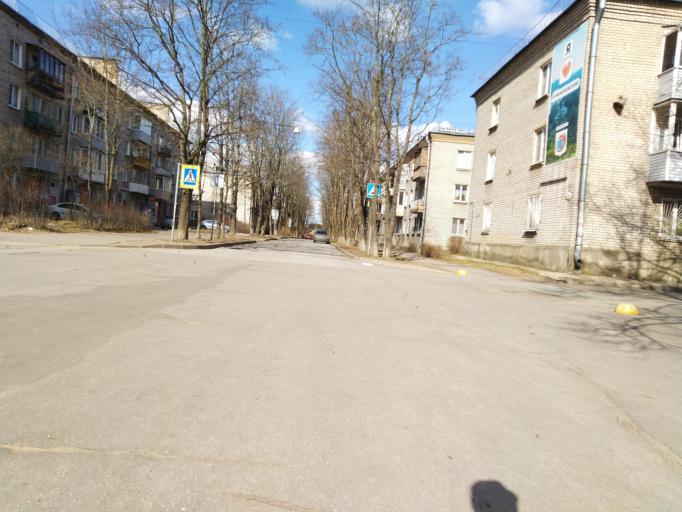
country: RU
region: Leningrad
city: Novoye Devyatkino
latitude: 60.1095
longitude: 30.4954
